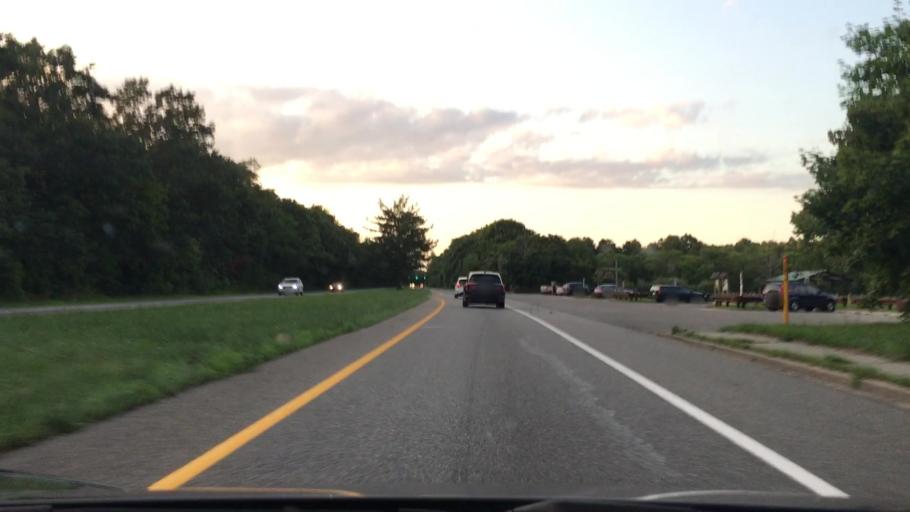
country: US
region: New York
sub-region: Suffolk County
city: Deer Park
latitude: 40.7758
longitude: -73.3104
